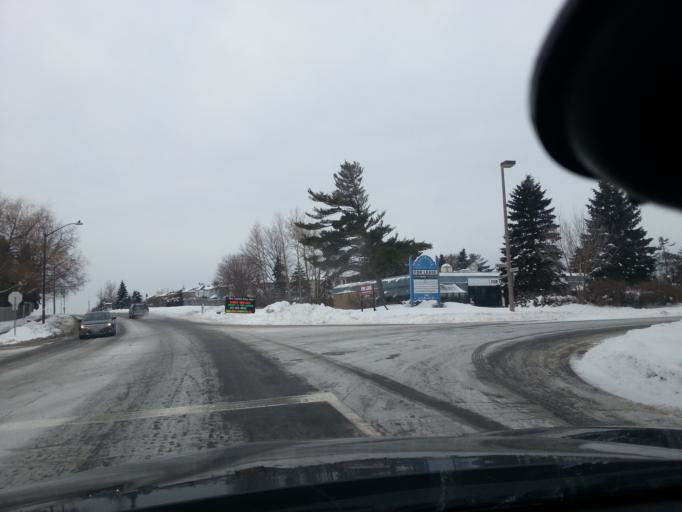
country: CA
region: Ontario
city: Bells Corners
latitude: 45.3050
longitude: -75.9048
